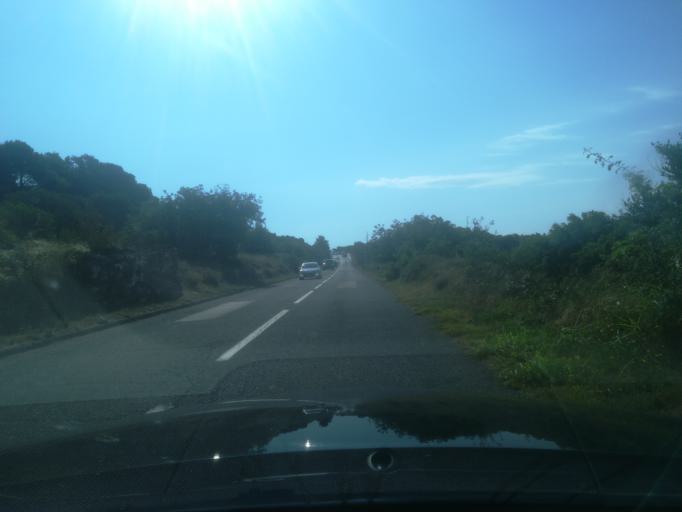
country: HR
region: Primorsko-Goranska
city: Banjol
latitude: 44.7077
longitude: 14.8357
